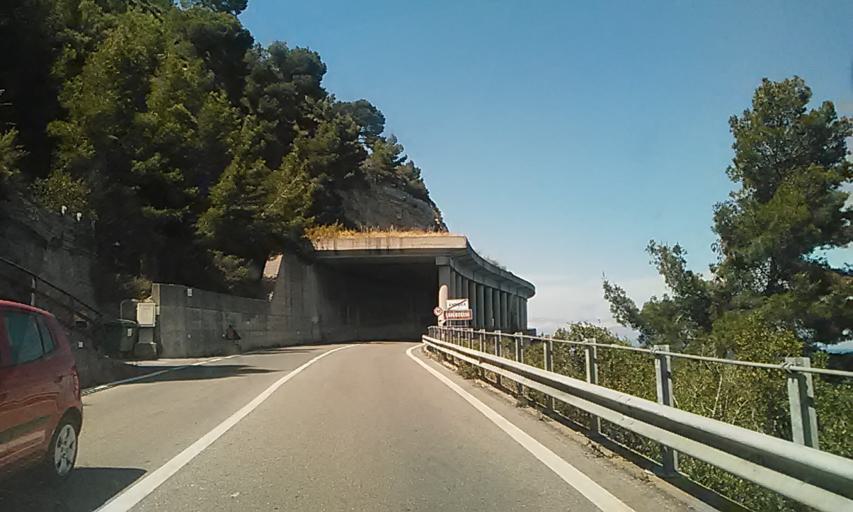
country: IT
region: Liguria
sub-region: Provincia di Savona
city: Marina di Andora
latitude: 43.9556
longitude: 8.1725
